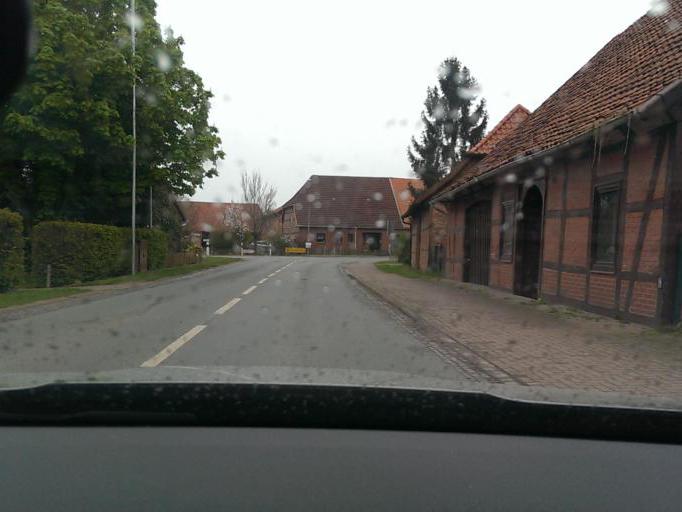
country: DE
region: Lower Saxony
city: Gilten
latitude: 52.6397
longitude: 9.5022
